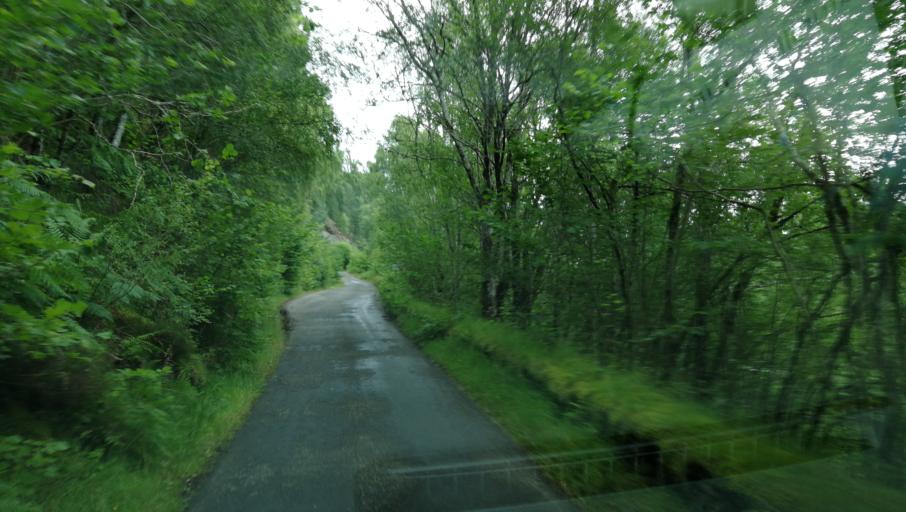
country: GB
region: Scotland
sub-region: Highland
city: Beauly
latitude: 57.3162
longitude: -4.8353
